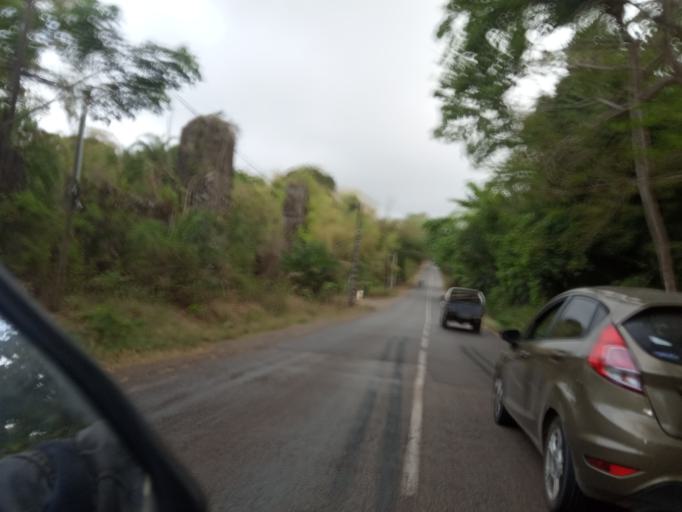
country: YT
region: Dembeni
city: Dembeni
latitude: -12.8627
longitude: 45.1980
